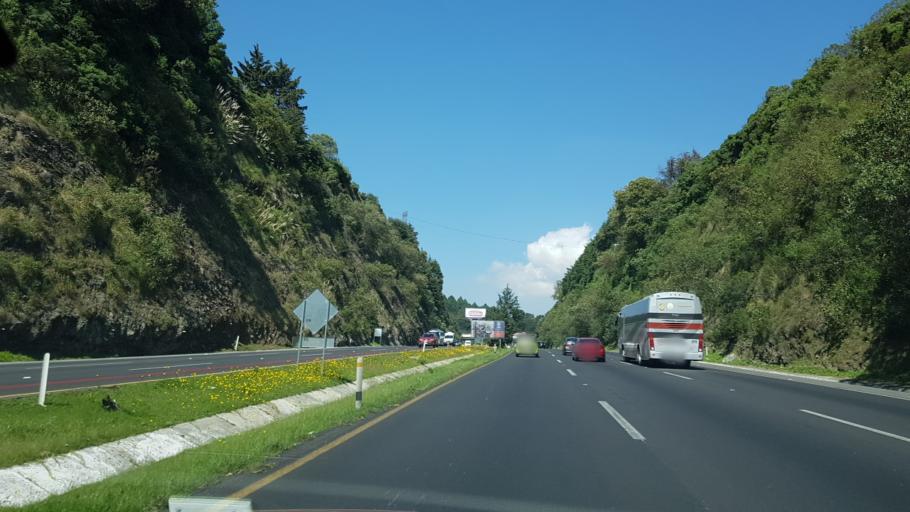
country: MX
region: Mexico City
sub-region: Cuajimalpa de Morelos
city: San Lorenzo Acopilco
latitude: 19.3184
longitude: -99.3286
